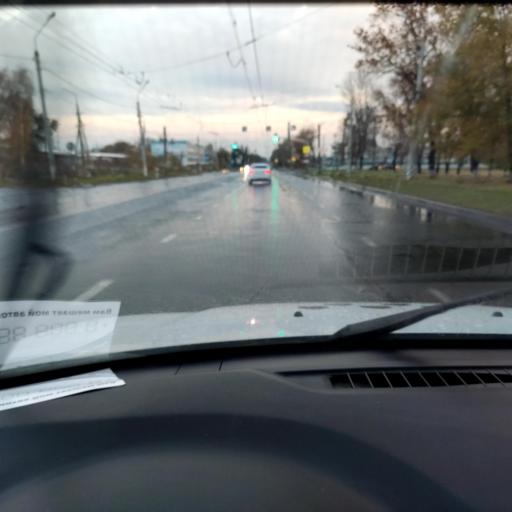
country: RU
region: Samara
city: Tol'yatti
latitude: 53.5340
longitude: 49.4398
